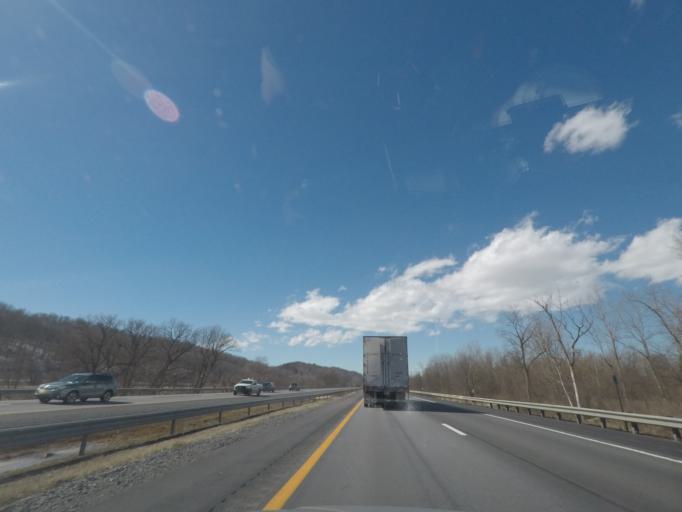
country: US
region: New York
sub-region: Montgomery County
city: Canajoharie
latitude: 42.9075
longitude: -74.5883
